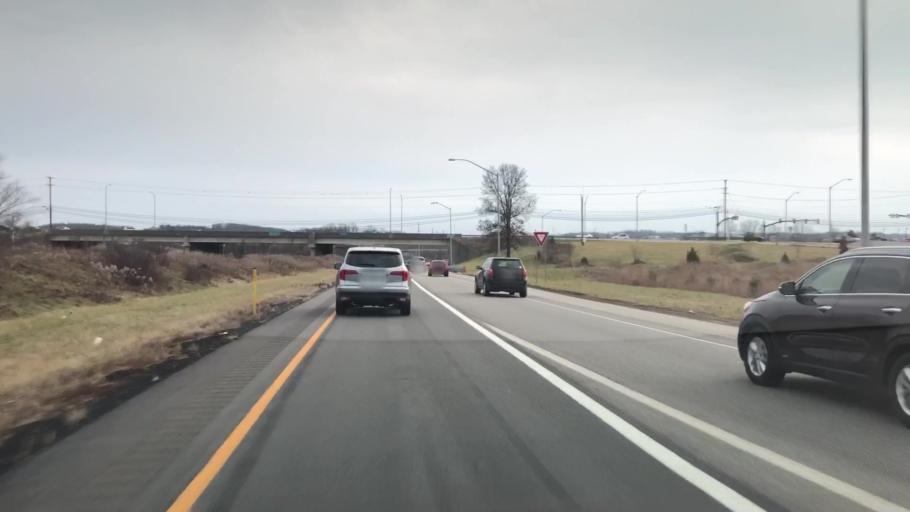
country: US
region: Pennsylvania
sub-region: Butler County
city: Cranberry Township
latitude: 40.6871
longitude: -80.0963
